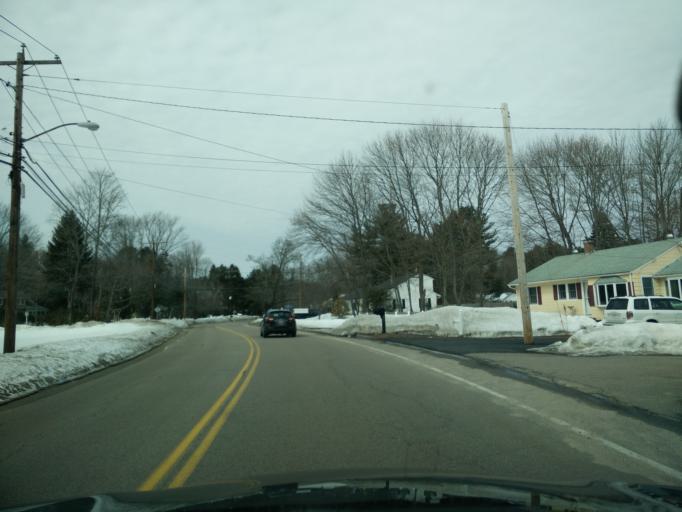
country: US
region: Massachusetts
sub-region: Norfolk County
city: Walpole
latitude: 42.1700
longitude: -71.2391
